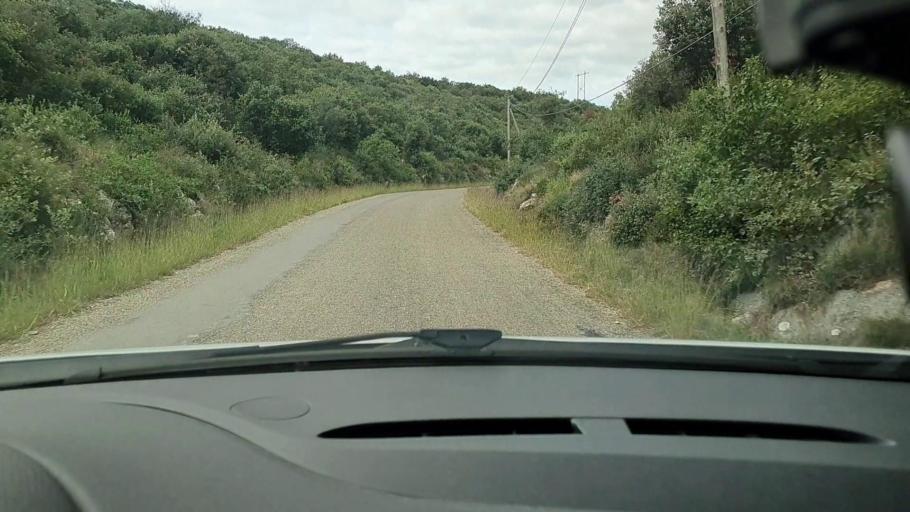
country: FR
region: Languedoc-Roussillon
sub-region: Departement du Gard
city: Montaren-et-Saint-Mediers
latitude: 44.0616
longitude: 4.3192
